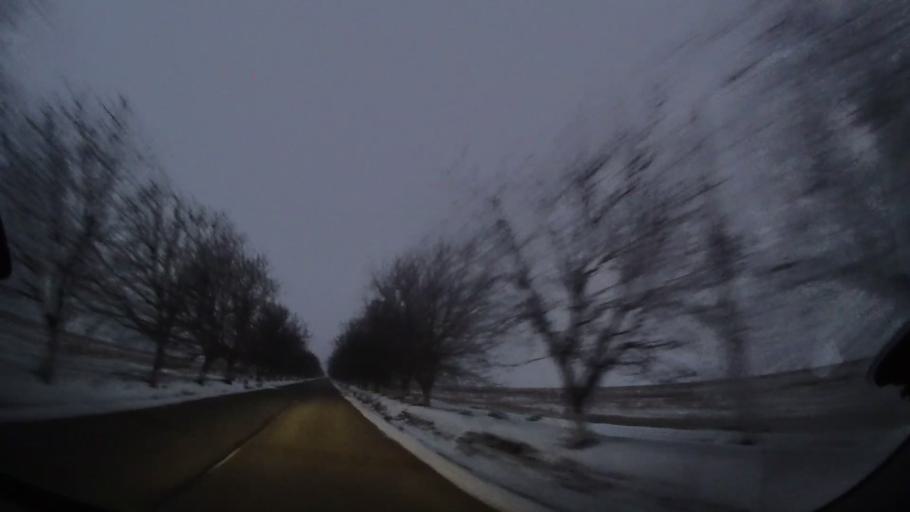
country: RO
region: Vaslui
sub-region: Comuna Dimitrie Cantemir
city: Dimitrie Cantemir
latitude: 46.5173
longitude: 28.0293
